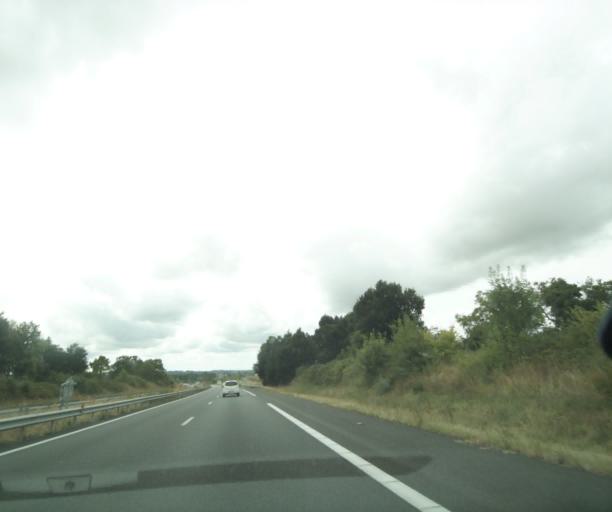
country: FR
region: Poitou-Charentes
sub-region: Departement de la Charente-Maritime
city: Mirambeau
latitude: 45.3904
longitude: -0.6045
